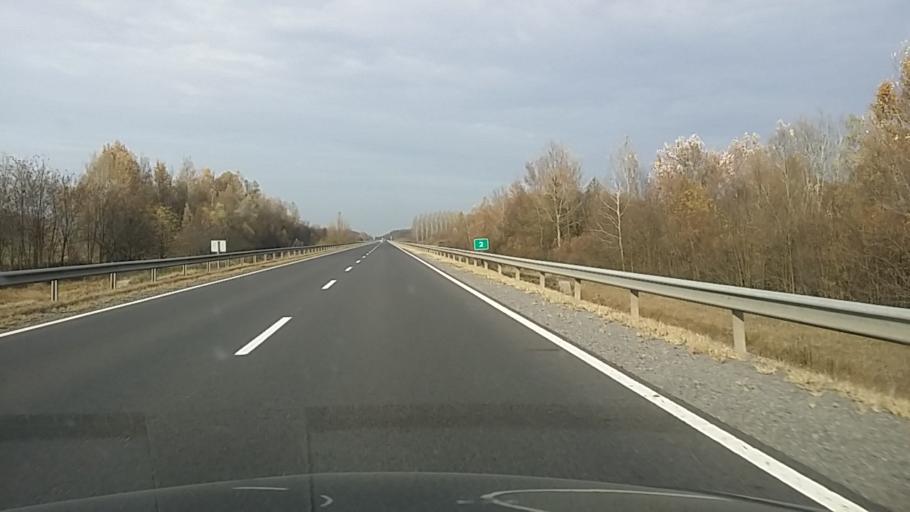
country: HU
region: Szabolcs-Szatmar-Bereg
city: Nagykallo
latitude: 47.9106
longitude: 21.8184
